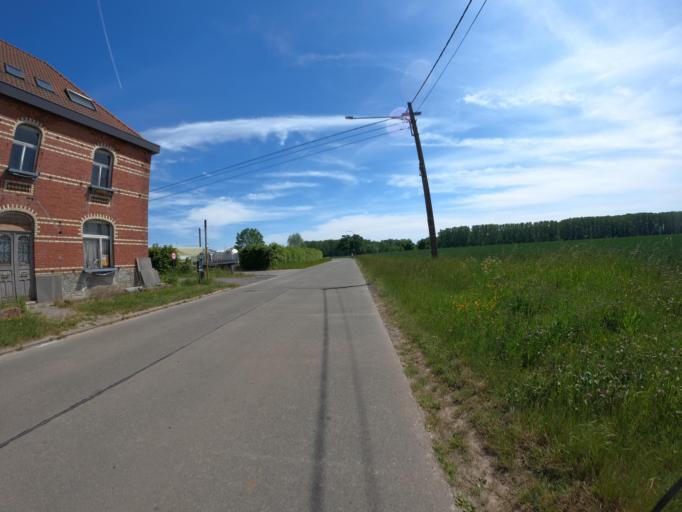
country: BE
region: Flanders
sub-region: Provincie Oost-Vlaanderen
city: Oosterzele
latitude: 50.9310
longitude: 3.7383
